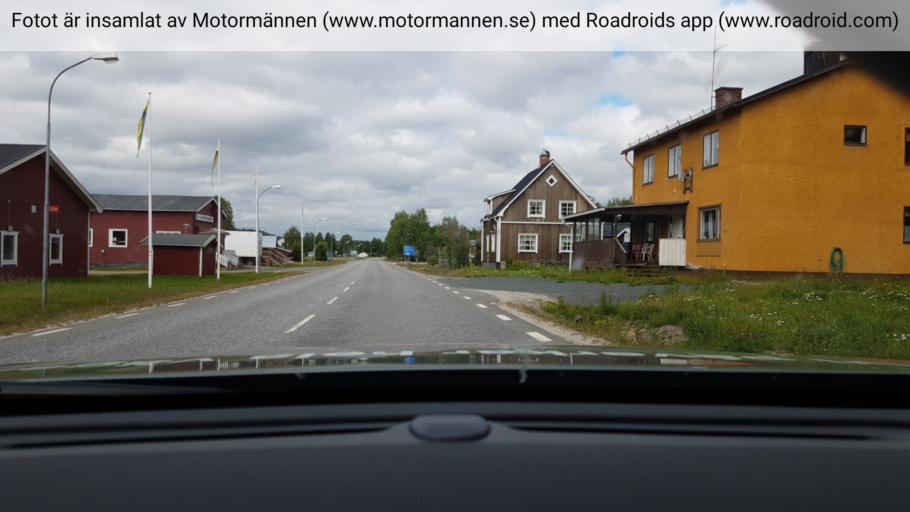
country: SE
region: Vaesterbotten
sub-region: Mala Kommun
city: Mala
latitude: 64.9872
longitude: 18.5190
